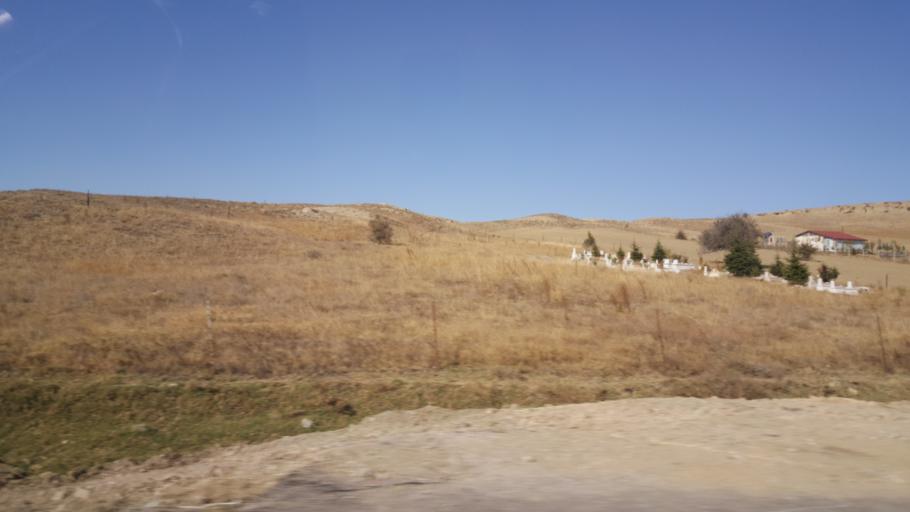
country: TR
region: Ankara
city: Haymana
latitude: 39.4749
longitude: 32.5448
